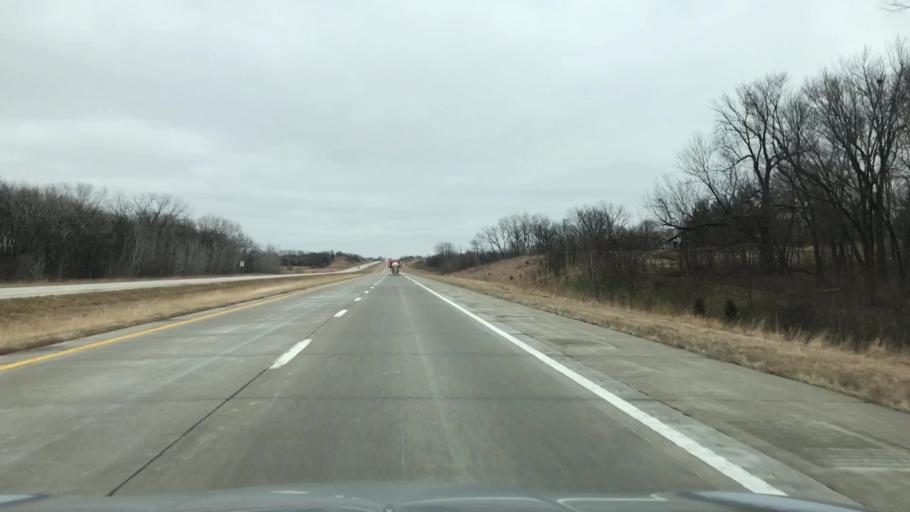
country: US
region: Missouri
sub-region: Caldwell County
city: Hamilton
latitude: 39.7342
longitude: -93.9688
